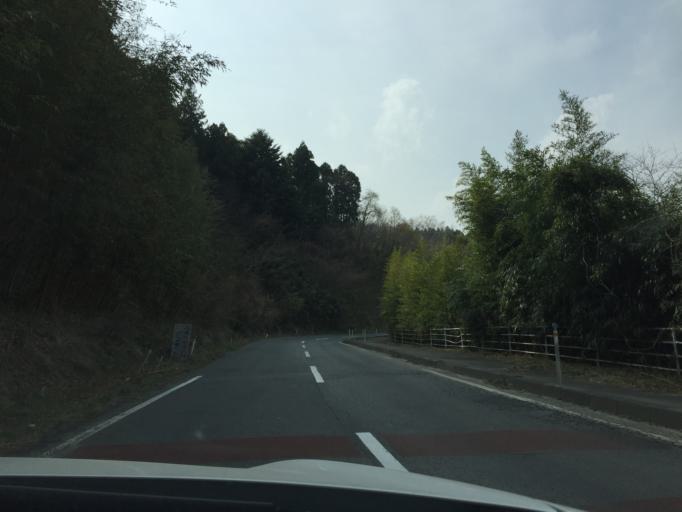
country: JP
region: Fukushima
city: Iwaki
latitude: 37.0166
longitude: 140.7355
